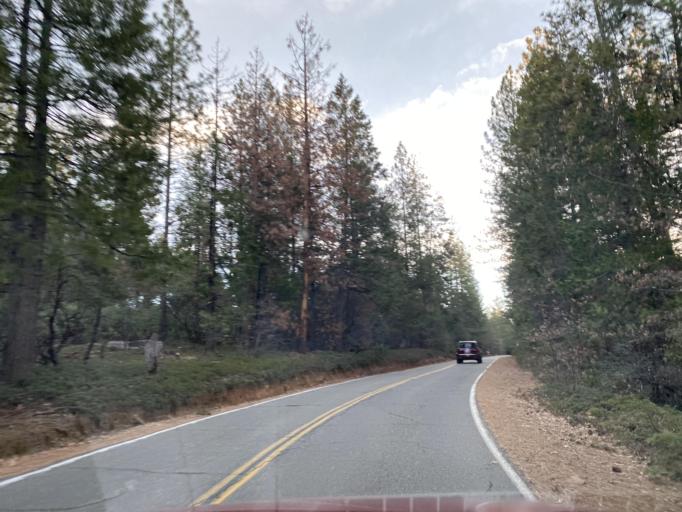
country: US
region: California
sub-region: Amador County
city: Pioneer
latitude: 38.5001
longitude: -120.6145
